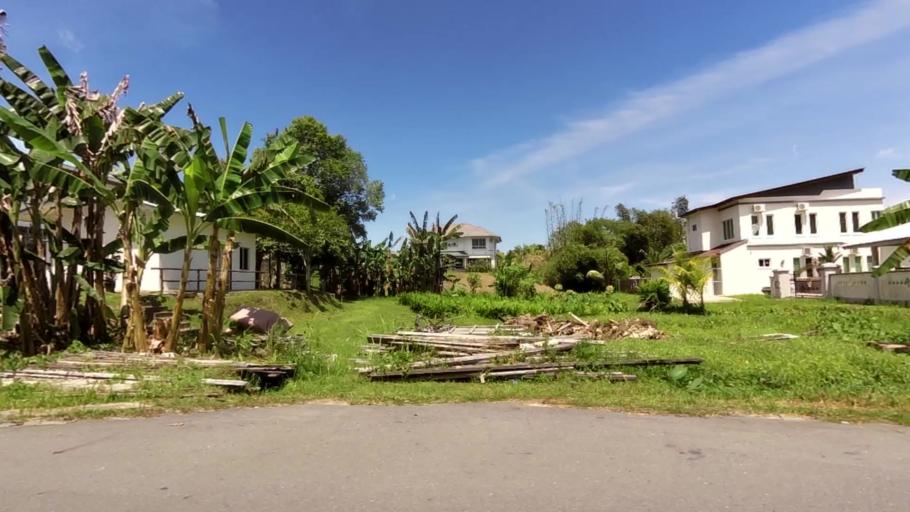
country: BN
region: Brunei and Muara
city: Bandar Seri Begawan
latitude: 4.9346
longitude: 114.9531
